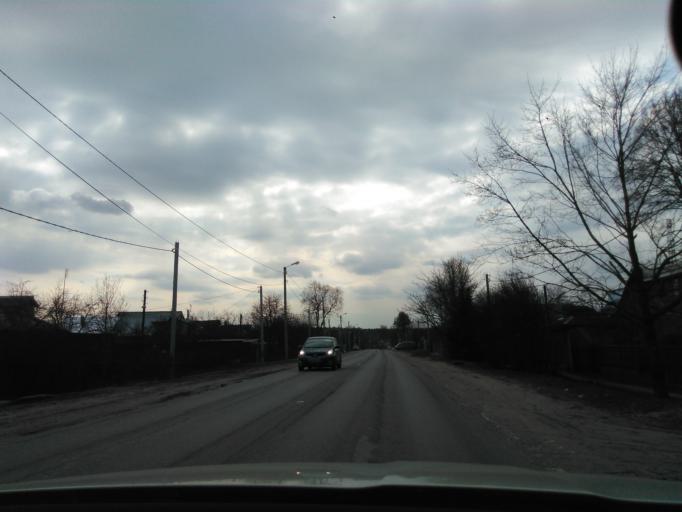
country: RU
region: Moskovskaya
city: Marfino
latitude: 56.0514
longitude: 37.5332
